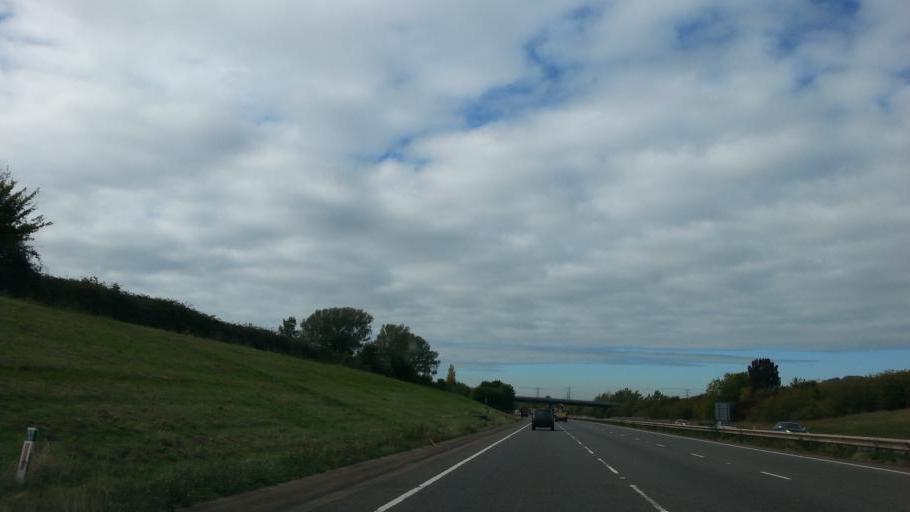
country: GB
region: England
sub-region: Gloucestershire
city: Churchdown
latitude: 51.8535
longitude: -2.1526
